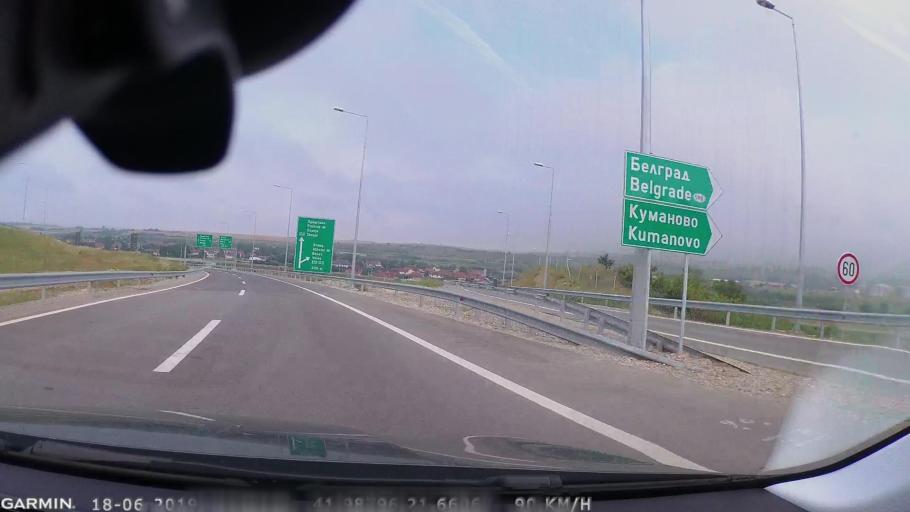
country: MK
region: Petrovec
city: Sredno Konjare
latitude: 41.9504
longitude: 21.7657
